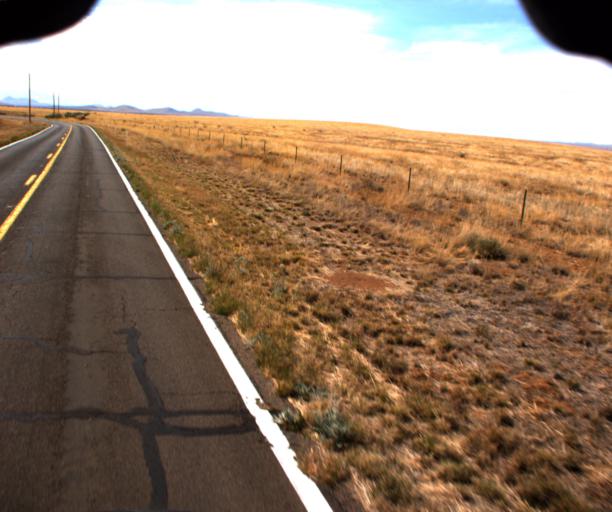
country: US
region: Arizona
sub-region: Cochise County
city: Willcox
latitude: 31.9923
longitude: -109.4461
